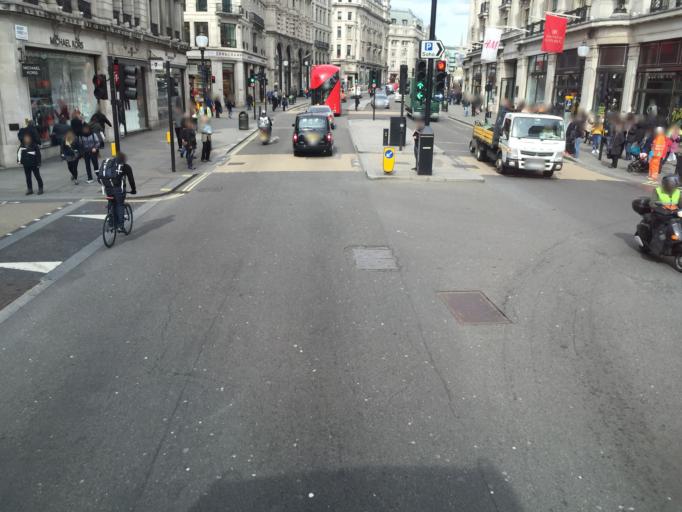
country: GB
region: England
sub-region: Greater London
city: London
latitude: 51.5135
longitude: -0.1412
